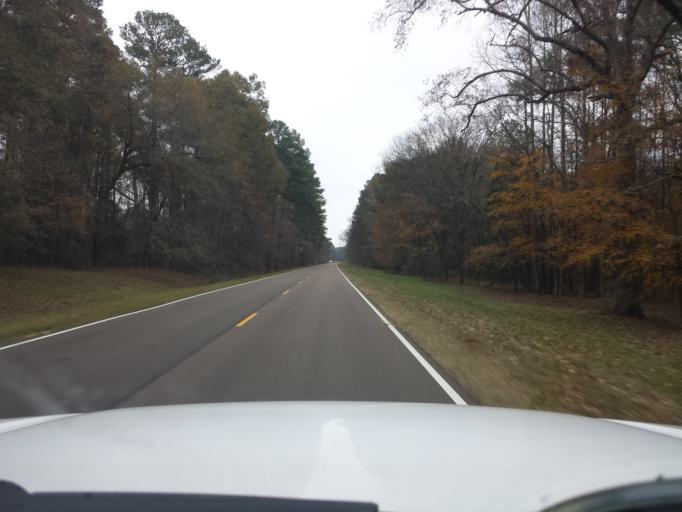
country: US
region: Mississippi
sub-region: Madison County
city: Canton
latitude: 32.5408
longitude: -89.9524
